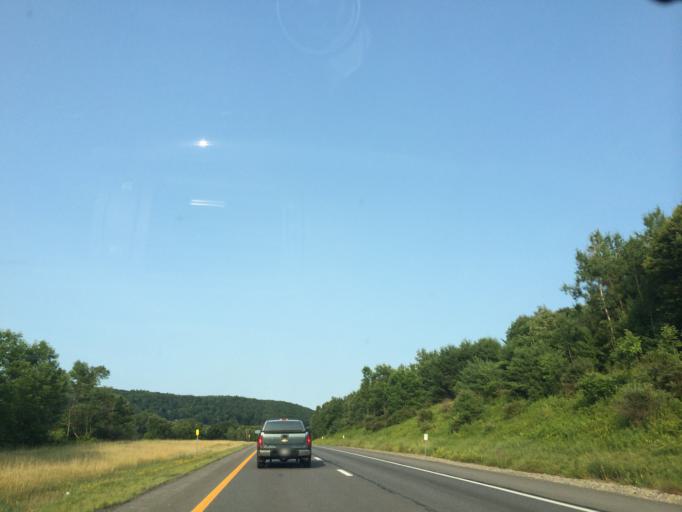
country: US
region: New York
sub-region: Columbia County
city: Chatham
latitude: 42.3888
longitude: -73.4868
